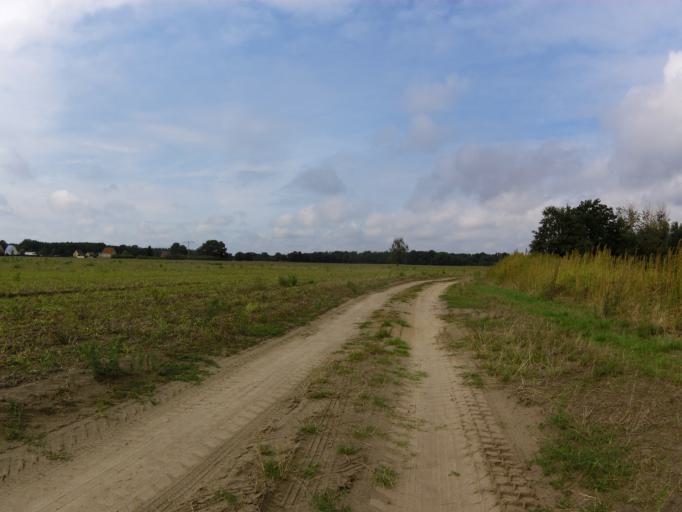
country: DE
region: Brandenburg
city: Storkow
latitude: 52.2696
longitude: 13.9344
